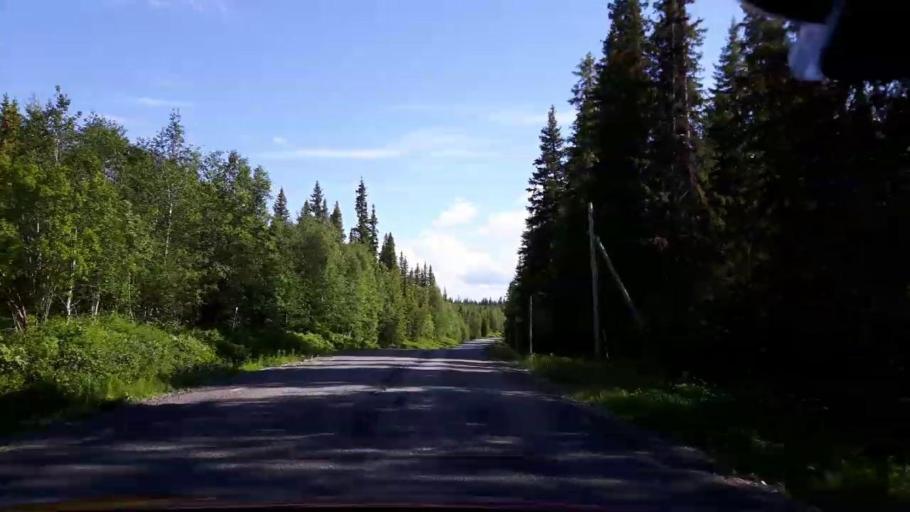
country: SE
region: Jaemtland
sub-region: Krokoms Kommun
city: Valla
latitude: 63.7452
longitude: 14.1189
